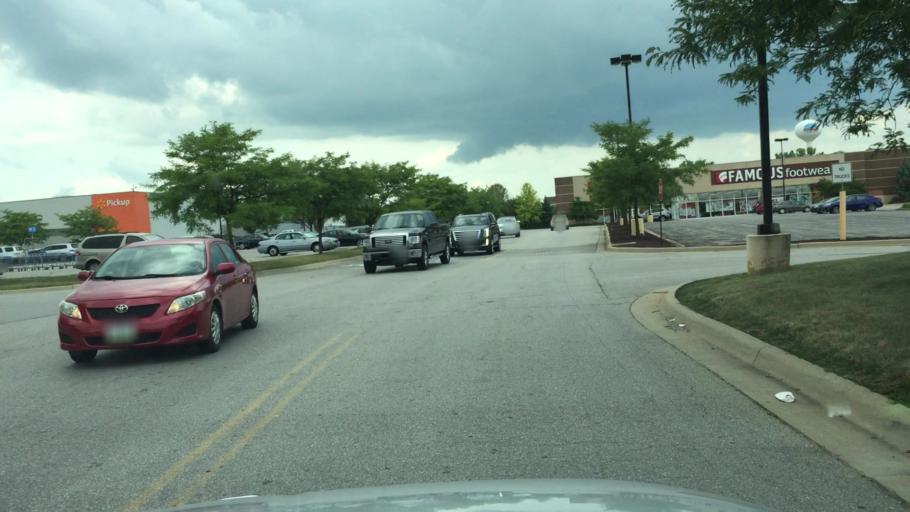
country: US
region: Iowa
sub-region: Johnson County
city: Coralville
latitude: 41.6961
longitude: -91.6109
